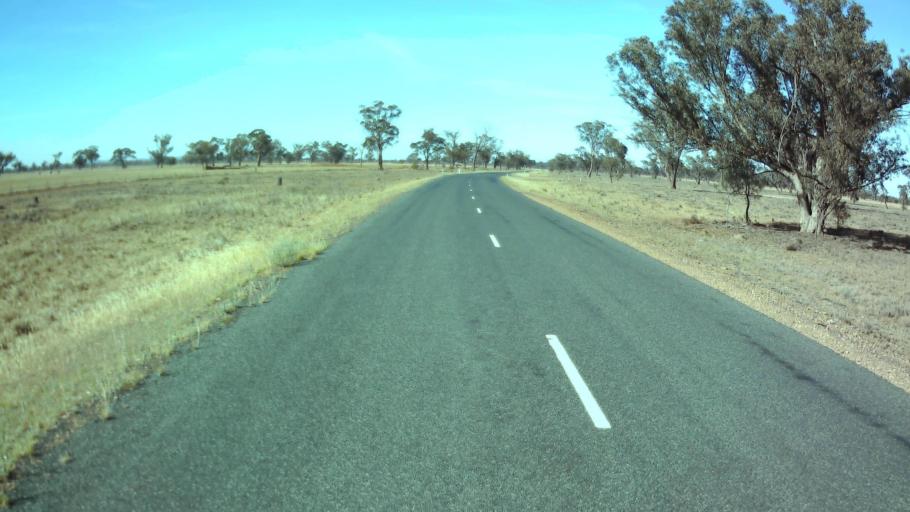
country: AU
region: New South Wales
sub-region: Weddin
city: Grenfell
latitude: -34.0689
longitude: 147.9052
